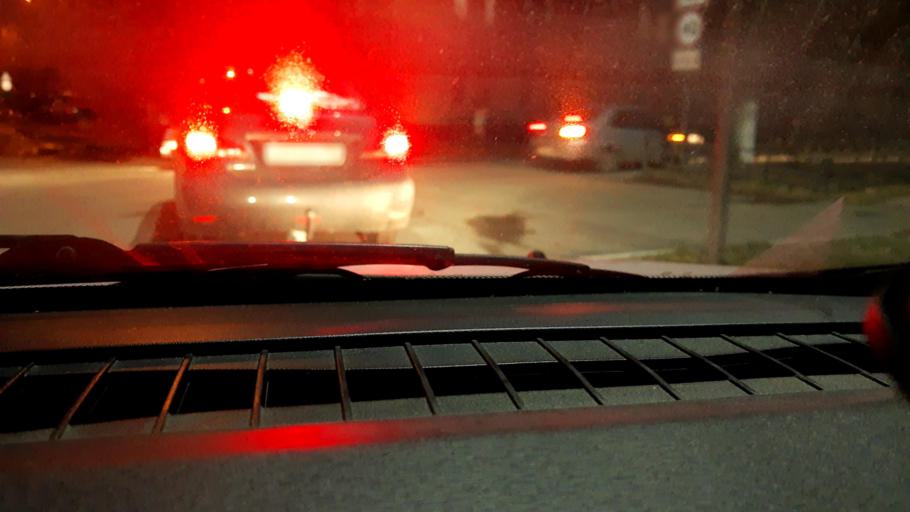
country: RU
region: Nizjnij Novgorod
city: Bor
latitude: 56.3571
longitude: 44.0655
